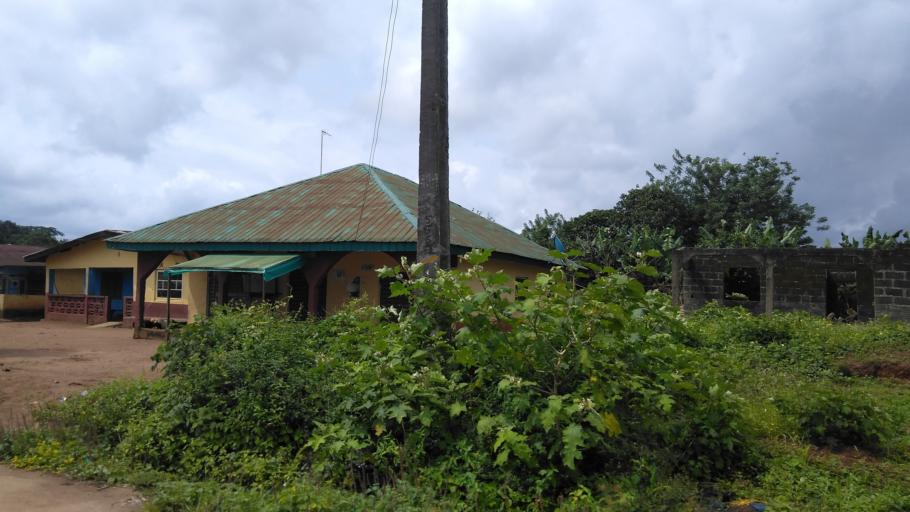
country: NG
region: Ogun
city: Abigi
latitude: 6.6025
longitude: 4.4898
